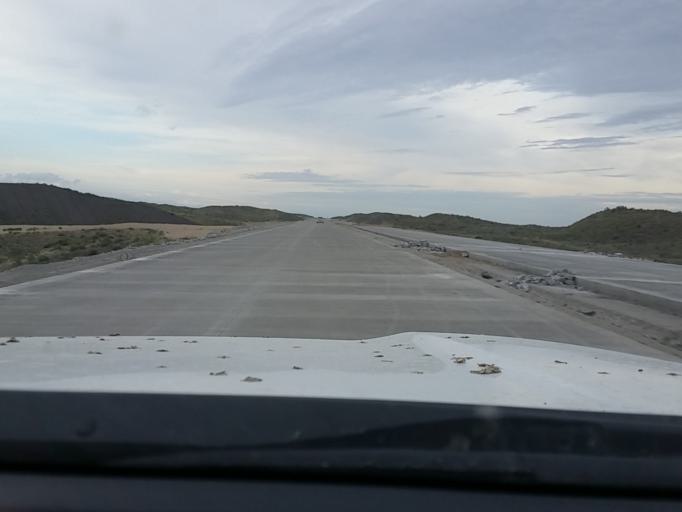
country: KZ
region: Almaty Oblysy
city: Zharkent
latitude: 44.1748
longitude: 80.2972
